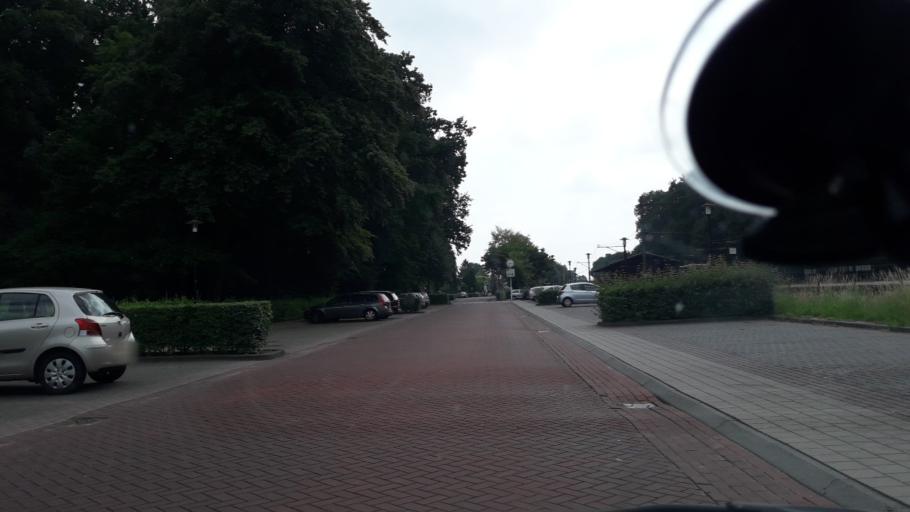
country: NL
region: Gelderland
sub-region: Gemeente Ermelo
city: Ermelo
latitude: 52.3024
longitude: 5.6156
